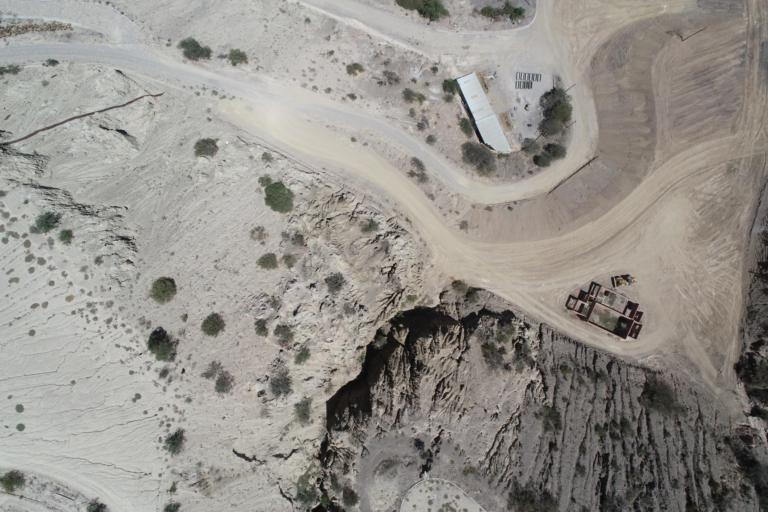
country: BO
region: La Paz
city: La Paz
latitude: -16.6169
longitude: -68.0601
